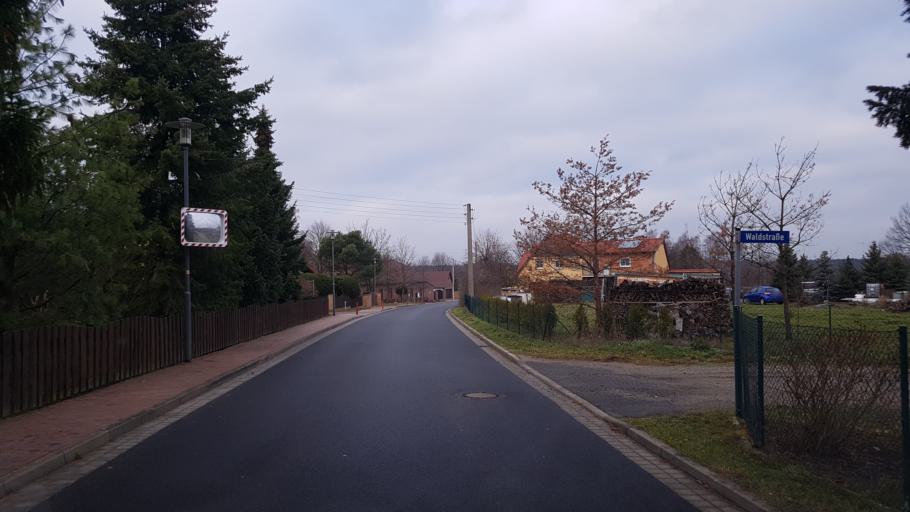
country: DE
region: Brandenburg
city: Sallgast
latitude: 51.5869
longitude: 13.8173
